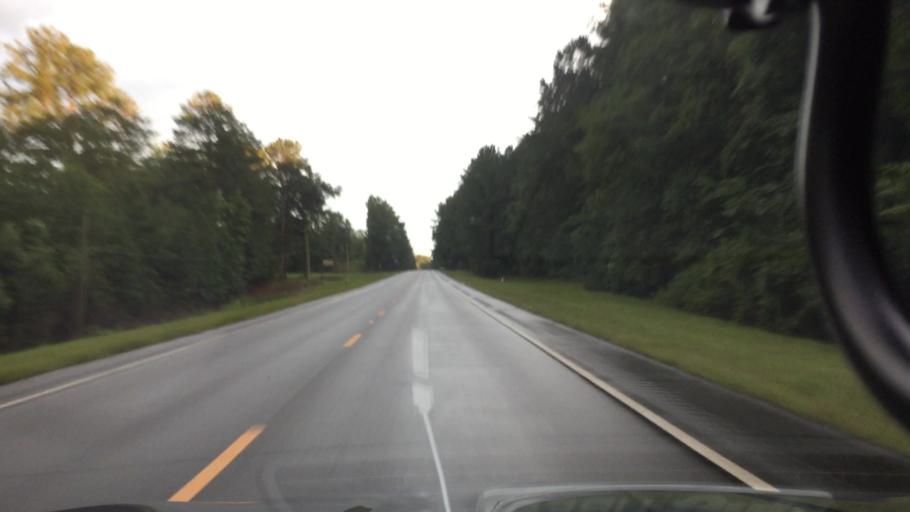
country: US
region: Alabama
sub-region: Coffee County
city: New Brockton
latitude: 31.5628
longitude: -85.9247
